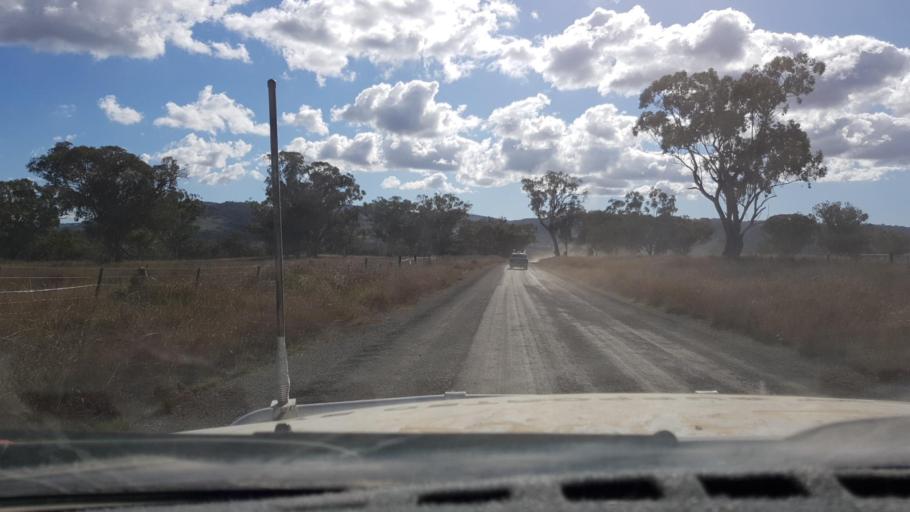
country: AU
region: New South Wales
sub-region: Tamworth Municipality
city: Manilla
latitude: -30.6297
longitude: 150.5088
